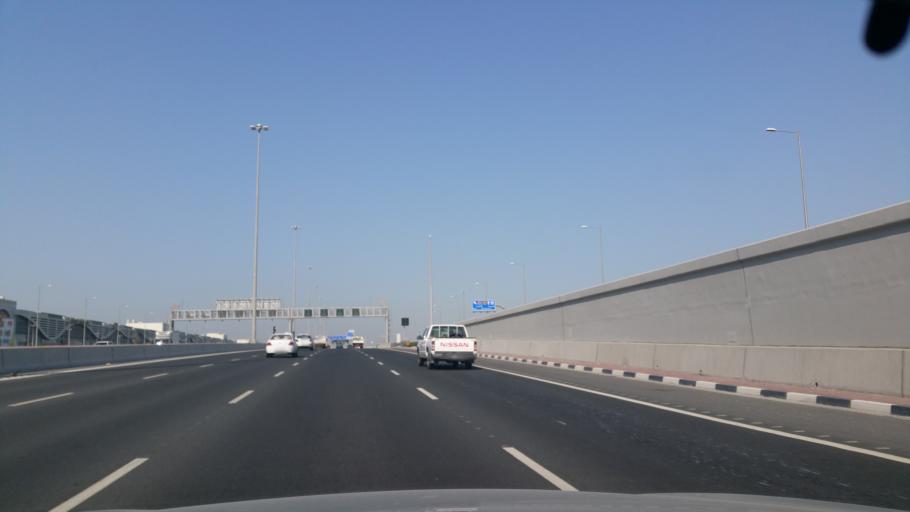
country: QA
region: Baladiyat ad Dawhah
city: Doha
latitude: 25.2137
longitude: 51.4997
